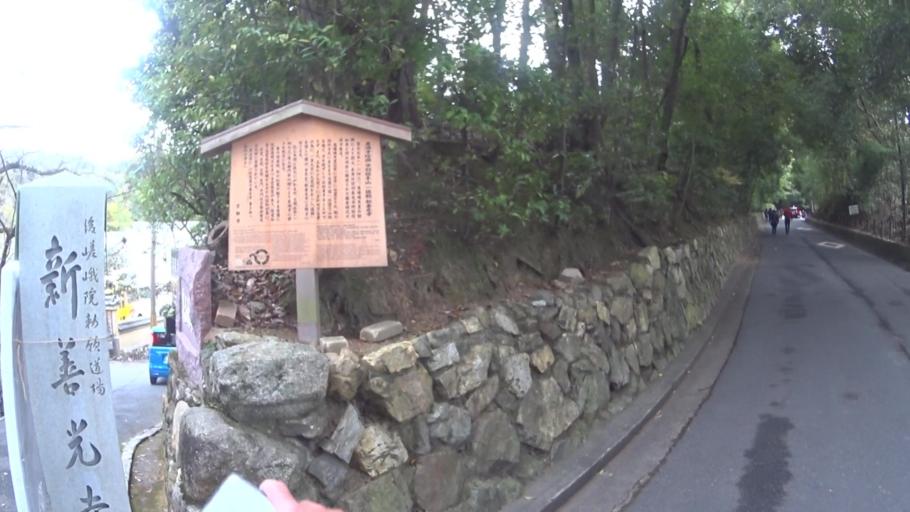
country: JP
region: Kyoto
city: Kyoto
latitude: 34.9803
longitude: 135.7783
